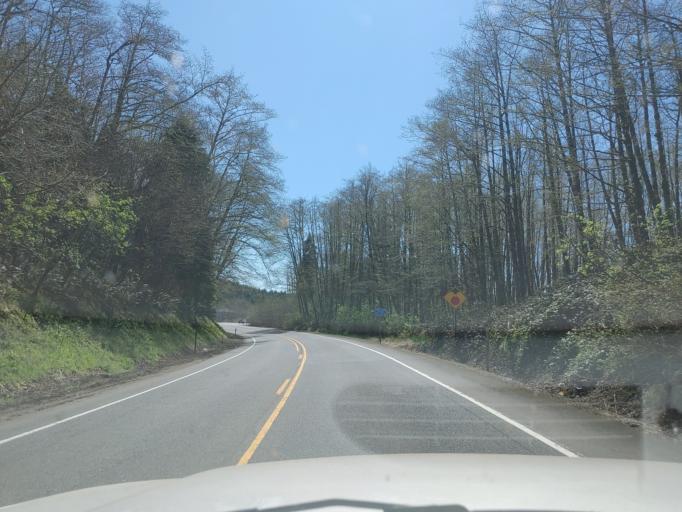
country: US
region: Oregon
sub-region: Clatsop County
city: Warrenton
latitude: 46.1470
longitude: -123.9023
